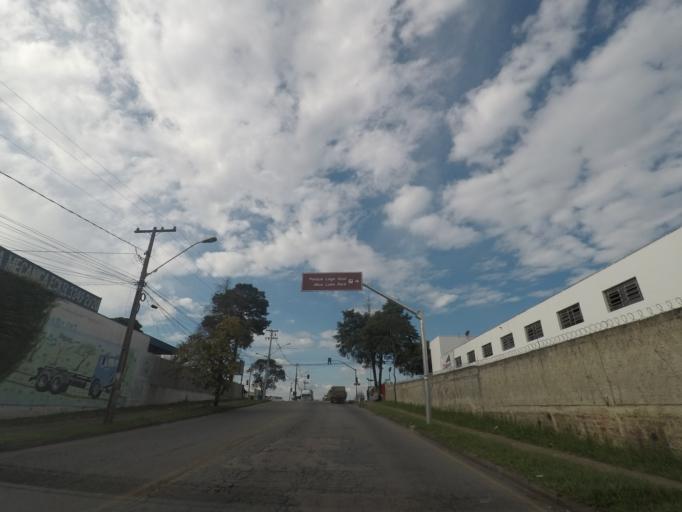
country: BR
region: Parana
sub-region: Sao Jose Dos Pinhais
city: Sao Jose dos Pinhais
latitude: -25.5327
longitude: -49.2979
